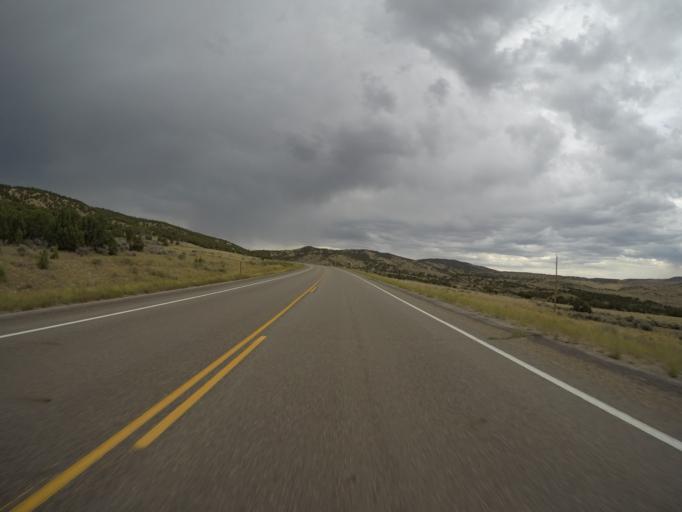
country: US
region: Colorado
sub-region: Rio Blanco County
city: Rangely
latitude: 40.3434
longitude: -108.4591
